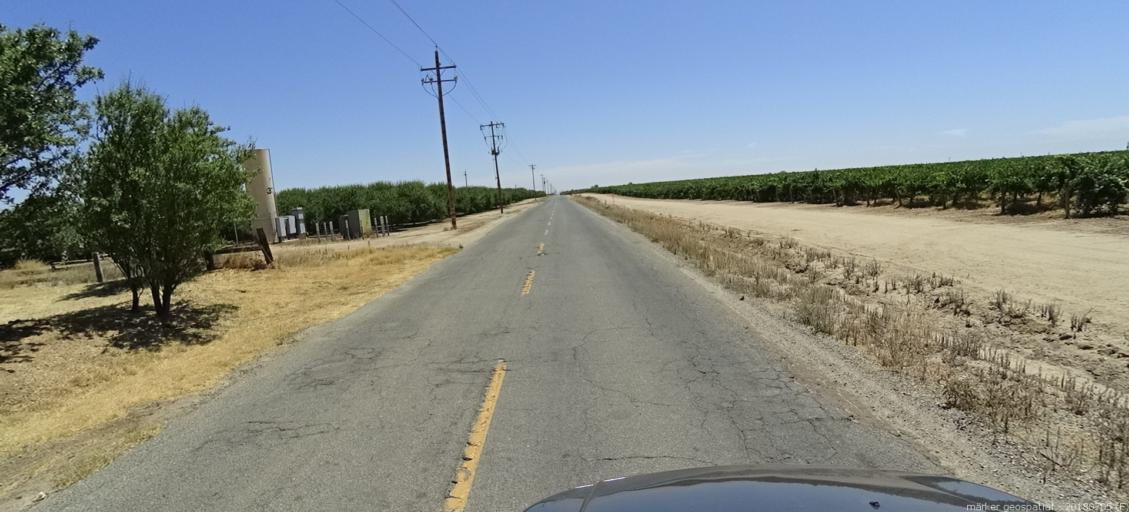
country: US
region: California
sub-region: Madera County
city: Fairmead
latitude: 37.0980
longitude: -120.1264
